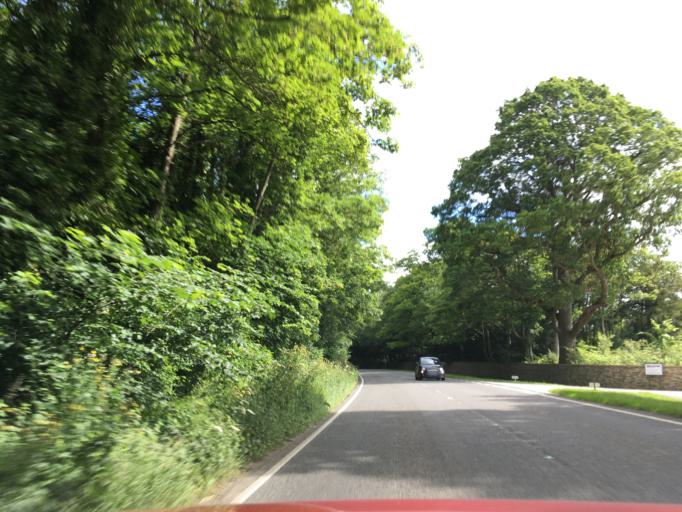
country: GB
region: England
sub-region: Gloucestershire
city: Lechlade
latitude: 51.7106
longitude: -1.6807
